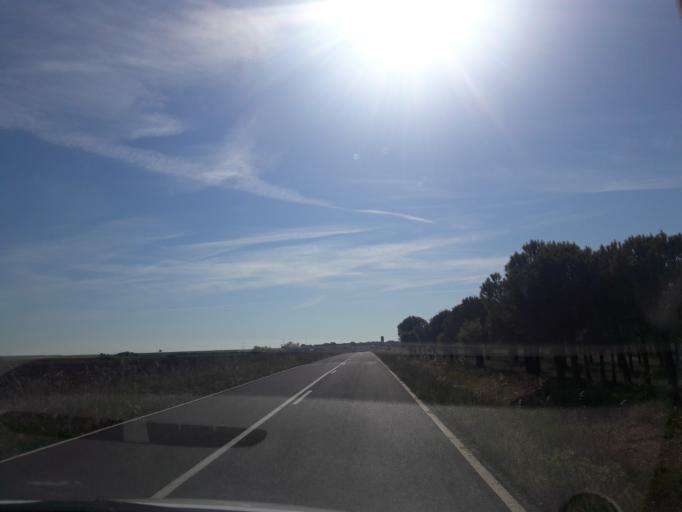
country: ES
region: Castille and Leon
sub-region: Provincia de Salamanca
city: Aldeanueva de Figueroa
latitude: 41.1374
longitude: -5.4936
